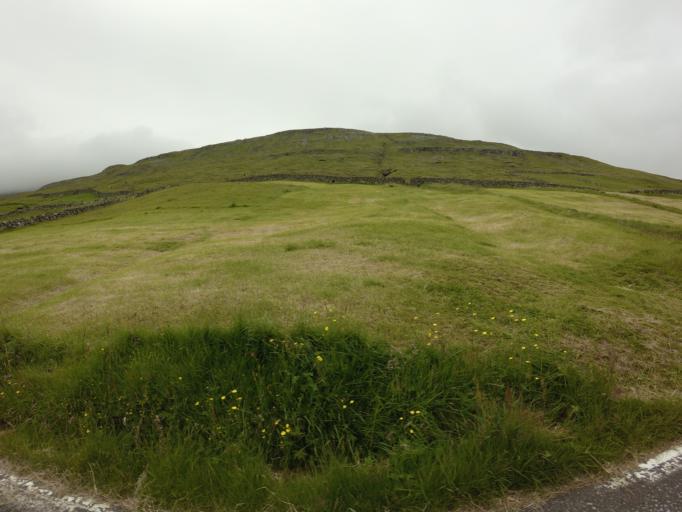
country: FO
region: Sandoy
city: Sandur
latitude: 61.8127
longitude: -6.6938
